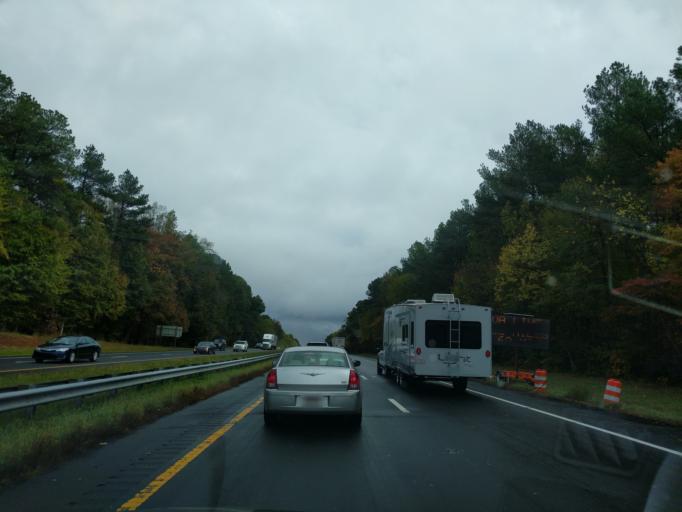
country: US
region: North Carolina
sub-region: Durham County
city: Durham
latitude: 36.0379
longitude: -78.9958
